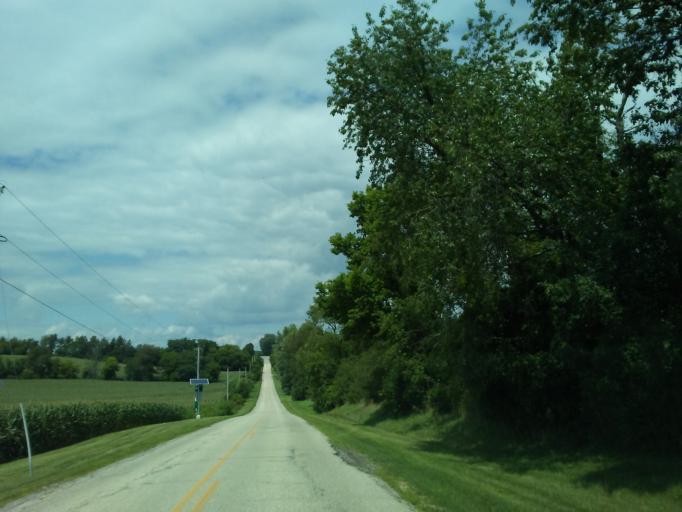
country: US
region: Wisconsin
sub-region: Dane County
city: Verona
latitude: 43.0058
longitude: -89.5781
